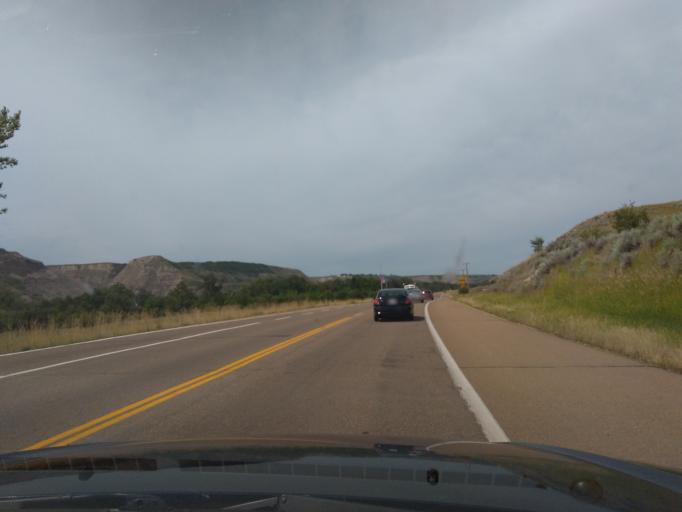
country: CA
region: Alberta
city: Three Hills
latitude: 51.4675
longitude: -112.7599
